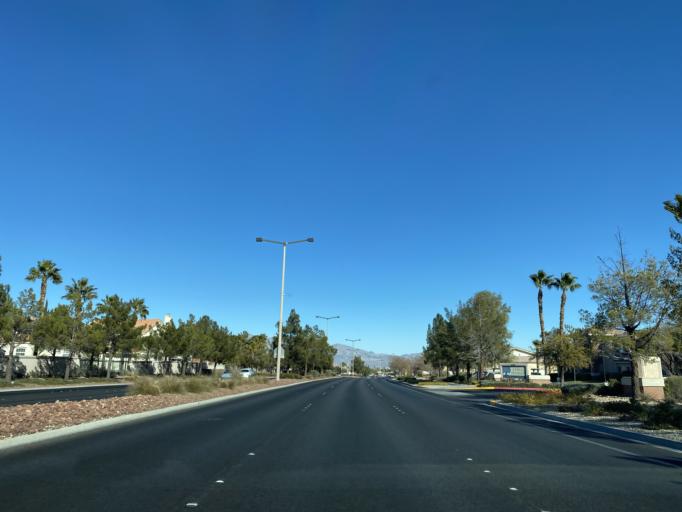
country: US
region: Nevada
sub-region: Clark County
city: Summerlin South
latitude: 36.1972
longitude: -115.2847
